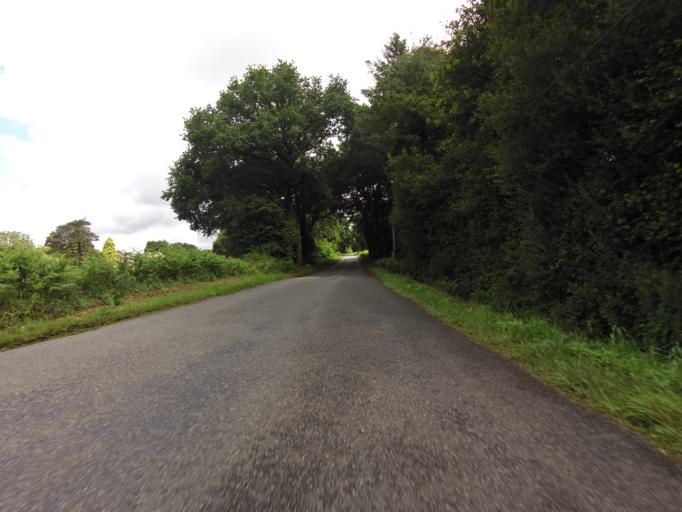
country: FR
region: Brittany
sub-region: Departement du Morbihan
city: Malansac
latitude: 47.7059
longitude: -2.2805
